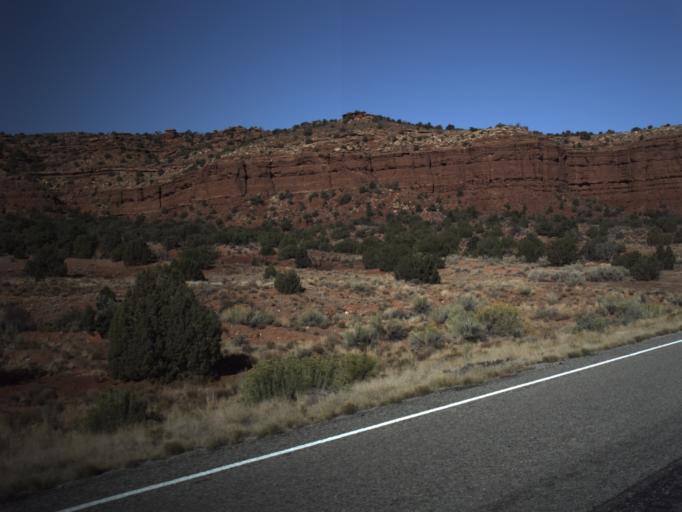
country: US
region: Utah
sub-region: San Juan County
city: Blanding
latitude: 37.6823
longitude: -110.2197
